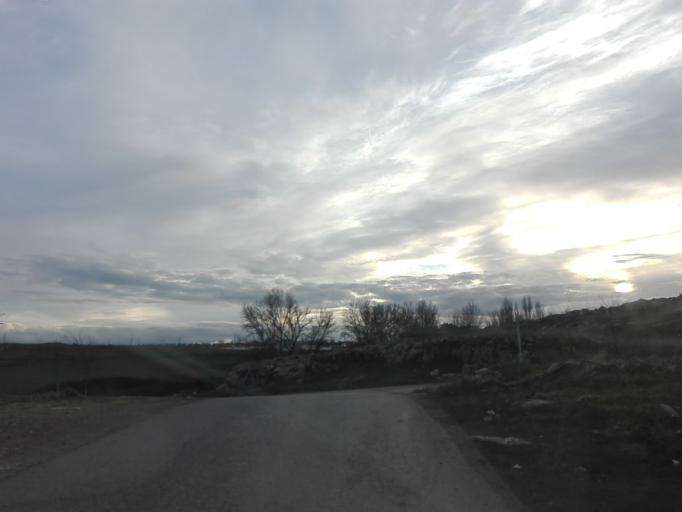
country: ES
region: Extremadura
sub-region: Provincia de Badajoz
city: Usagre
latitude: 38.3563
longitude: -6.1756
